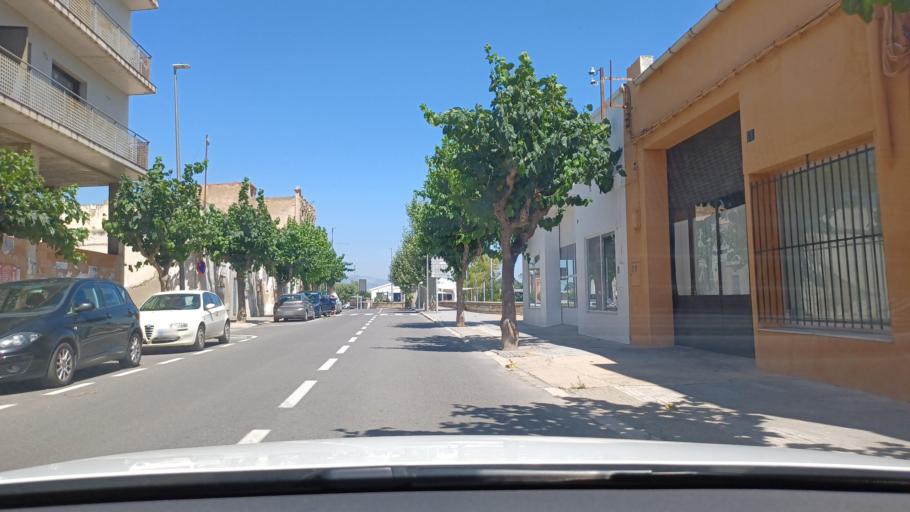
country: ES
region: Catalonia
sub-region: Provincia de Tarragona
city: Amposta
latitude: 40.7119
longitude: 0.5845
